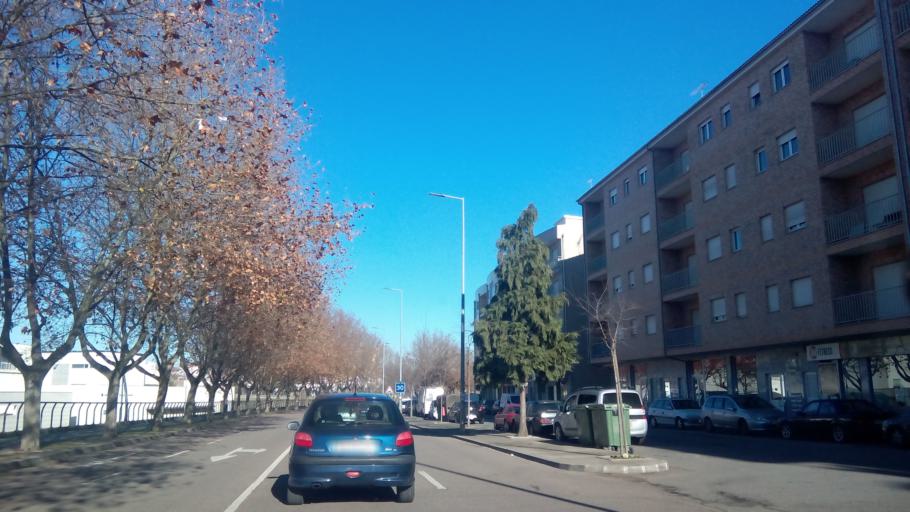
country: PT
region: Braganca
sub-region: Braganca Municipality
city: Braganca
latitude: 41.7928
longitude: -6.7693
